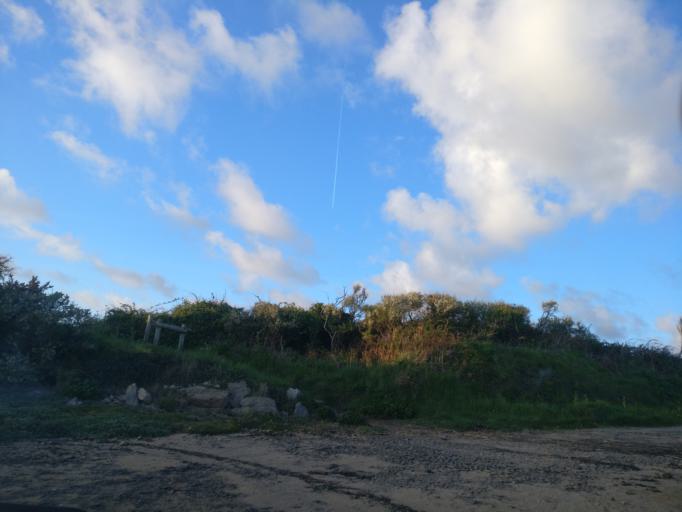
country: FR
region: Brittany
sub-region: Departement du Finistere
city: Lampaul-Plouarzel
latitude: 48.4667
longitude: -4.7544
